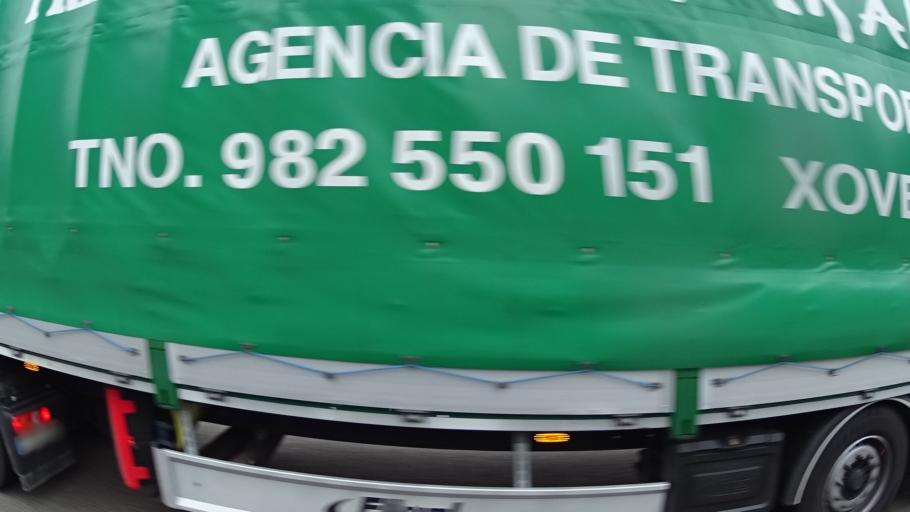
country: ES
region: Galicia
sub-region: Provincia de Lugo
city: Guitiriz
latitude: 43.1824
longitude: -7.8166
